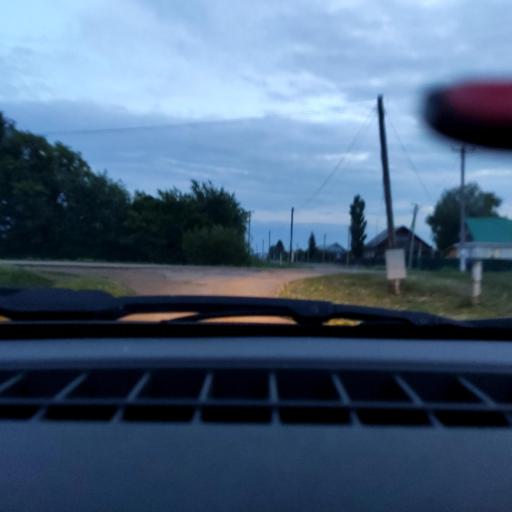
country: RU
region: Bashkortostan
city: Tolbazy
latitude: 54.2886
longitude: 55.8204
